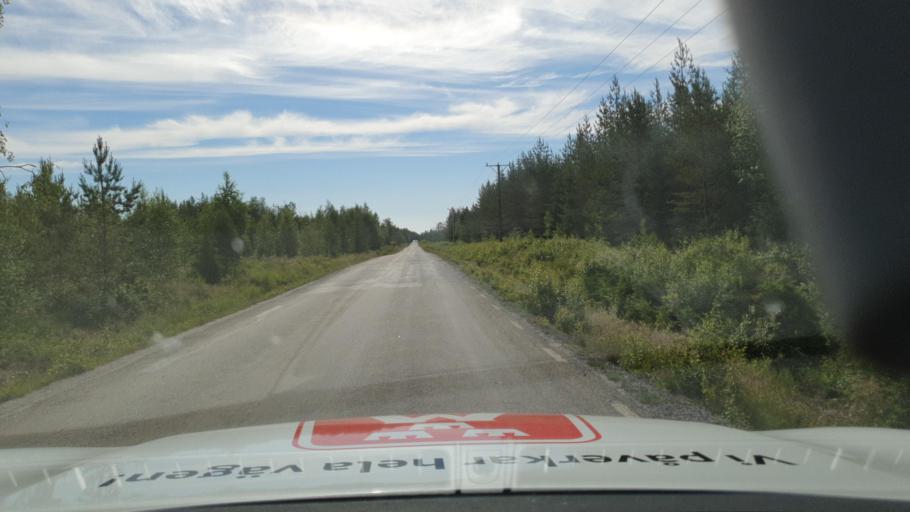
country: SE
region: Vaesterbotten
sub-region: Umea Kommun
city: Saevar
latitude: 63.8714
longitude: 20.7164
